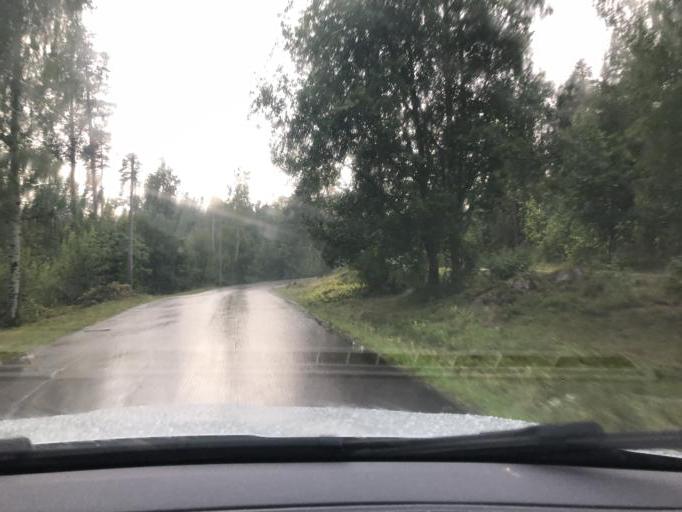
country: SE
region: Vaesternorrland
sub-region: Sundsvalls Kommun
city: Sundsvall
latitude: 62.4001
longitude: 17.3080
